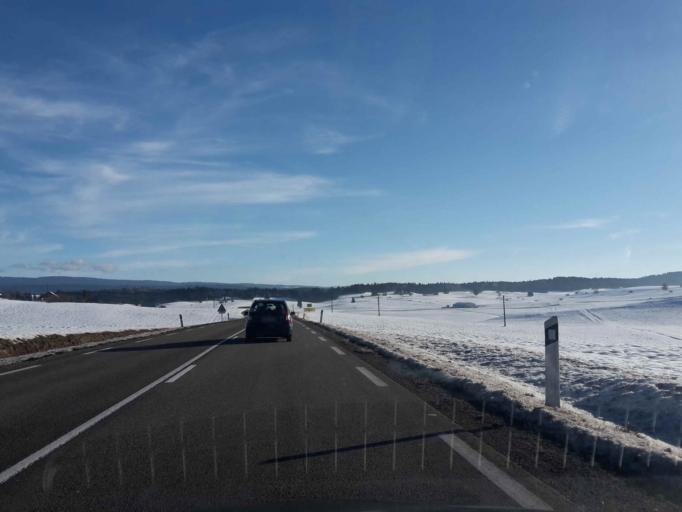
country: FR
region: Franche-Comte
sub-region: Departement du Doubs
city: Doubs
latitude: 46.9867
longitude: 6.3298
